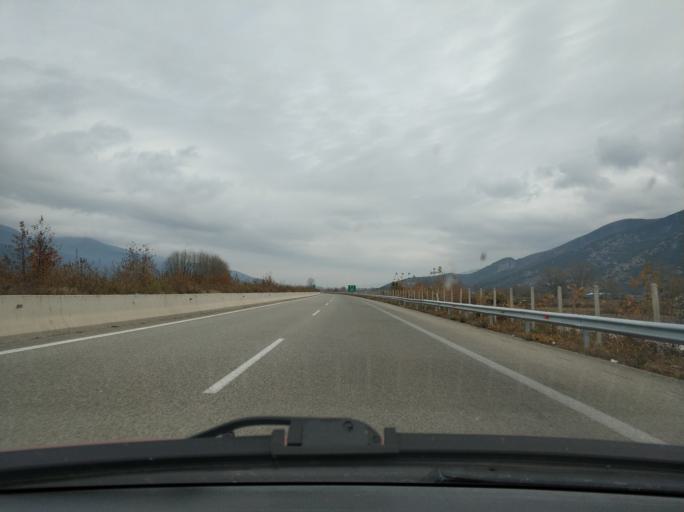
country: GR
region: East Macedonia and Thrace
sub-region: Nomos Kavalas
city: Nikisiani
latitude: 40.8304
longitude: 24.1014
